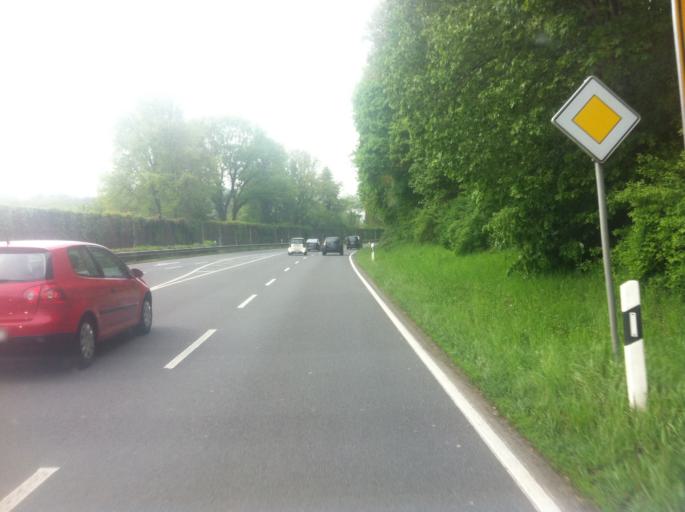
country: DE
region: North Rhine-Westphalia
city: Lohmar
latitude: 50.8559
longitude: 7.2182
